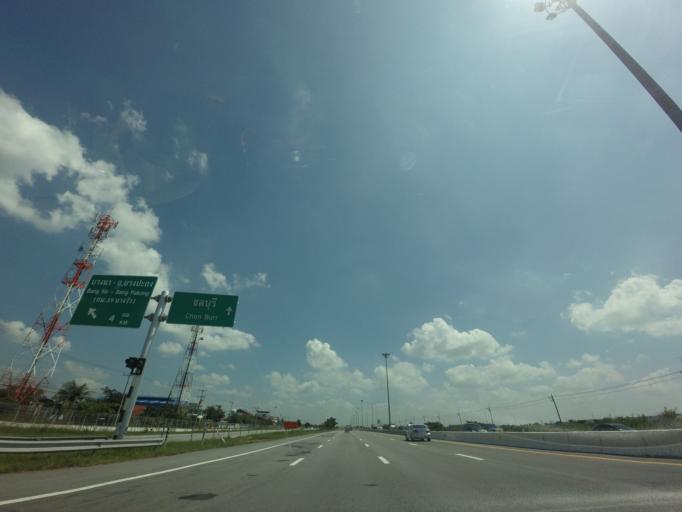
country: TH
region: Chachoengsao
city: Bang Pakong
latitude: 13.6052
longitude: 100.9449
